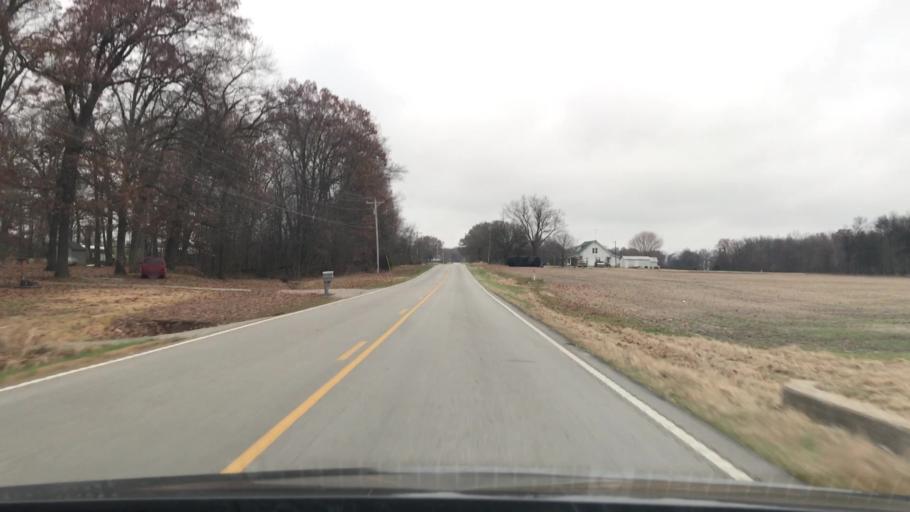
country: US
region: Kentucky
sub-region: Todd County
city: Guthrie
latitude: 36.7144
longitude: -87.1926
